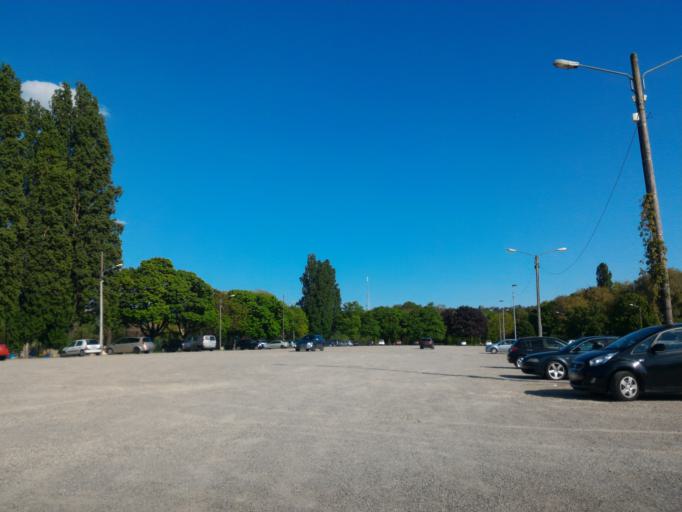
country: FR
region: Alsace
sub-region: Departement du Haut-Rhin
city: Mulhouse
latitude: 47.7400
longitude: 7.3213
